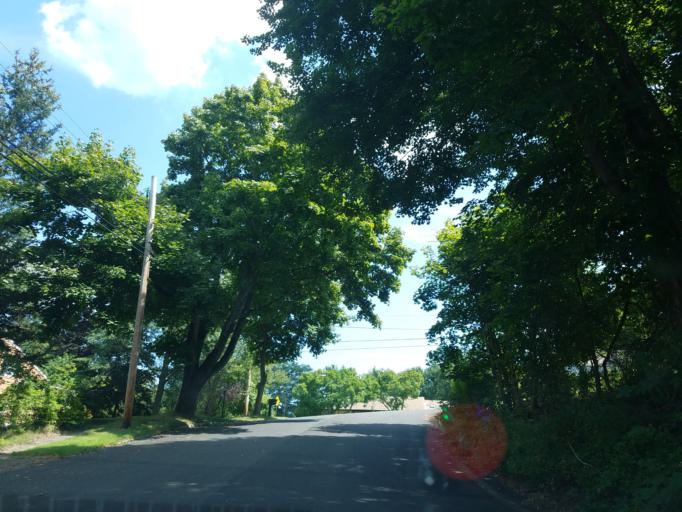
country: US
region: Connecticut
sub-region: New Haven County
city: Woodmont
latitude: 41.2260
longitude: -73.0201
